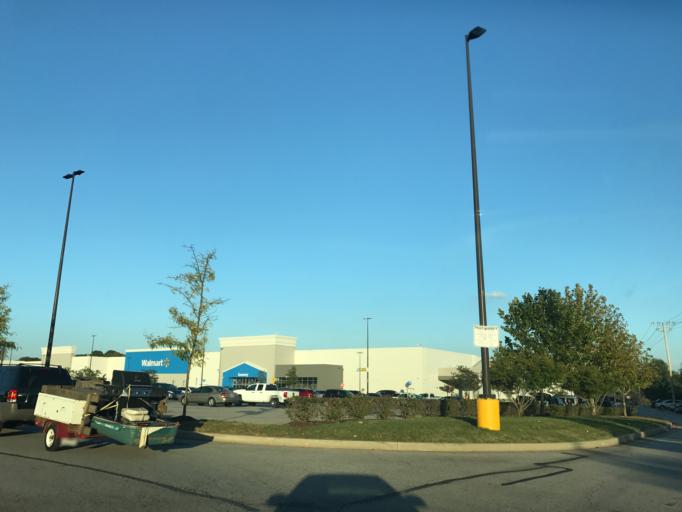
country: US
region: Maryland
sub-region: Baltimore County
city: Lansdowne
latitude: 39.2478
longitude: -76.6698
